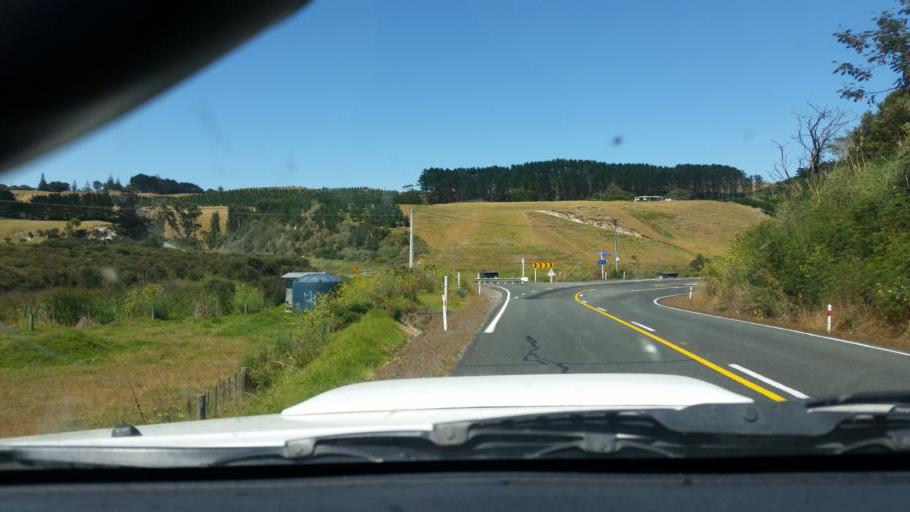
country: NZ
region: Northland
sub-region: Kaipara District
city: Dargaville
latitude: -35.8340
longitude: 173.6617
